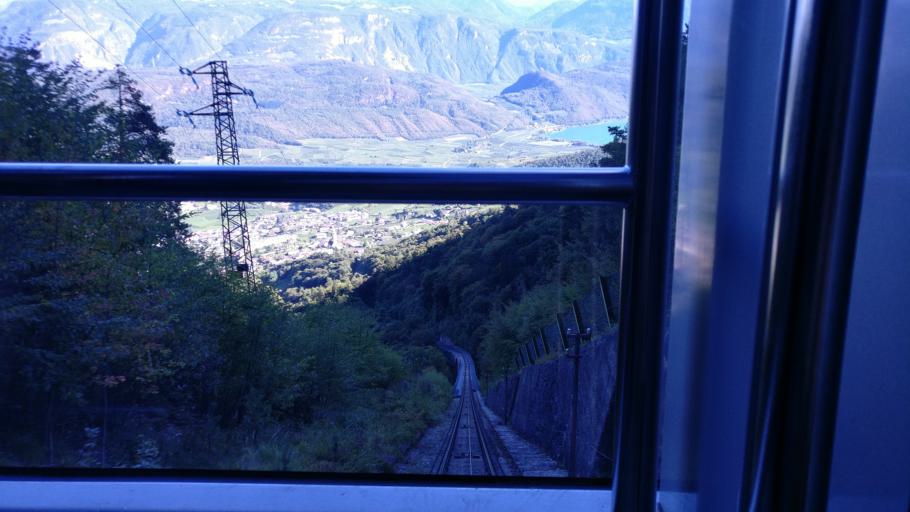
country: IT
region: Trentino-Alto Adige
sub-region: Bolzano
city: Caldaro sulla Strada del Vino
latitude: 46.4137
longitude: 11.2178
